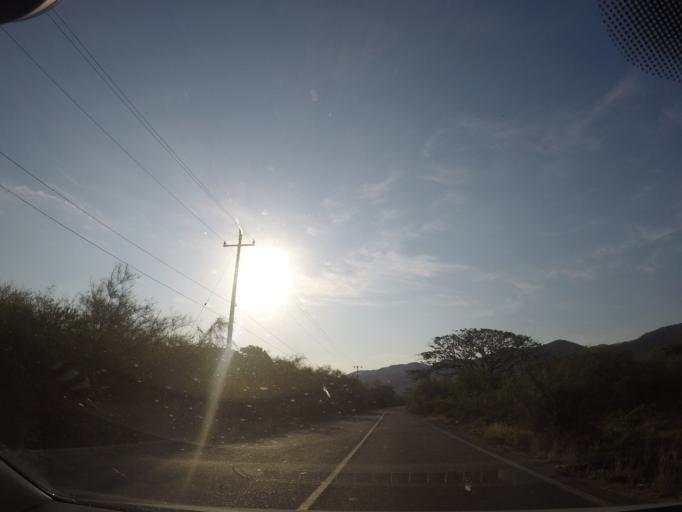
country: MX
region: Oaxaca
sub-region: Santo Domingo Tehuantepec
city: La Noria
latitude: 16.2310
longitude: -95.1823
